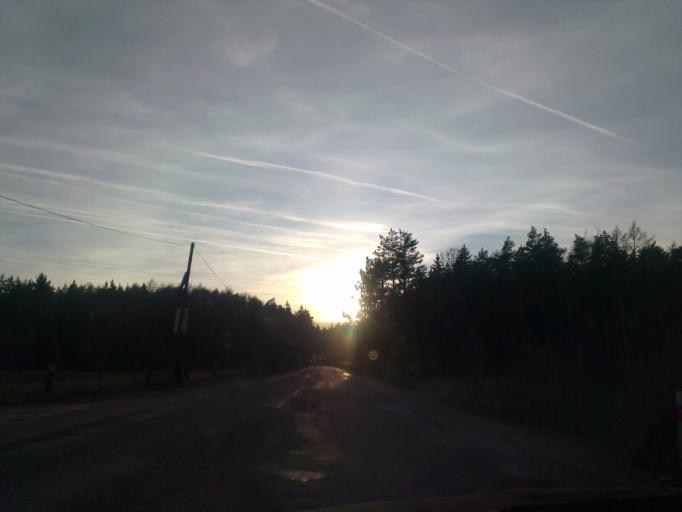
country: CZ
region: South Moravian
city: Bilovice nad Svitavou
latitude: 49.2479
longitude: 16.7292
